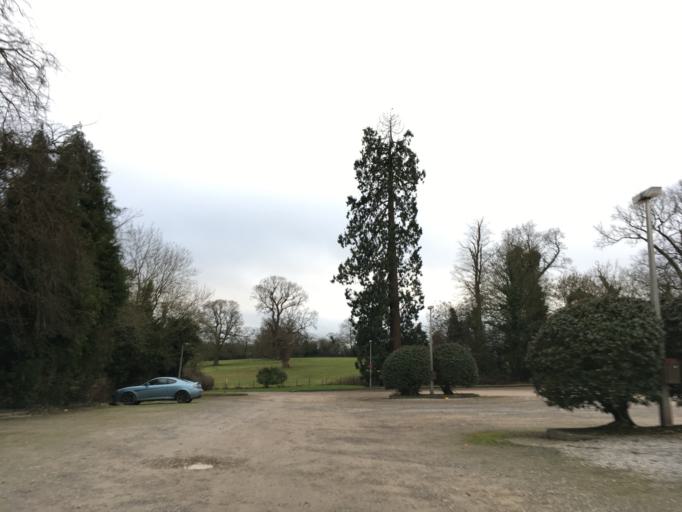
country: GB
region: England
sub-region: South Gloucestershire
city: Winterbourne
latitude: 51.5385
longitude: -2.5242
